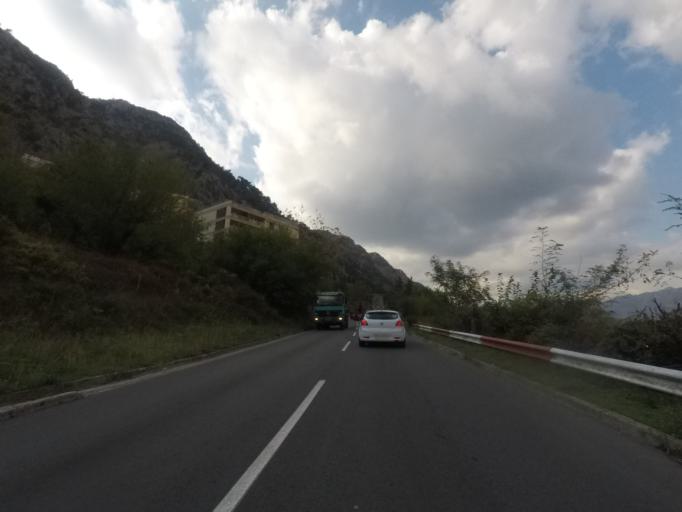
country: ME
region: Kotor
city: Kotor
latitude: 42.4176
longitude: 18.7616
